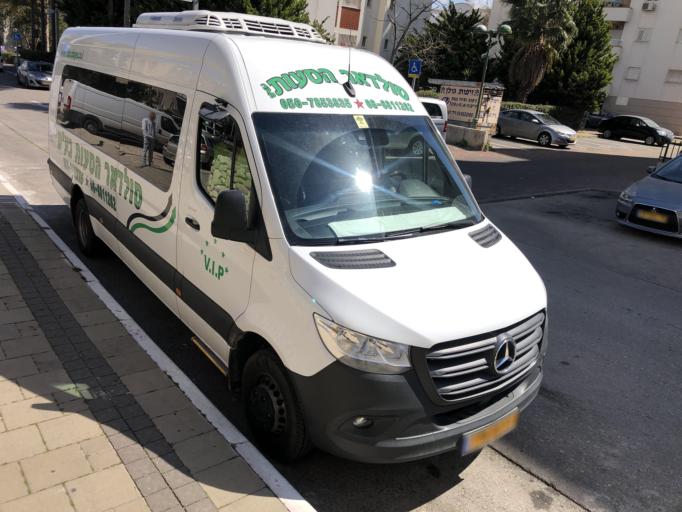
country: IL
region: Tel Aviv
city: Bat Yam
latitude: 32.0081
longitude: 34.7579
